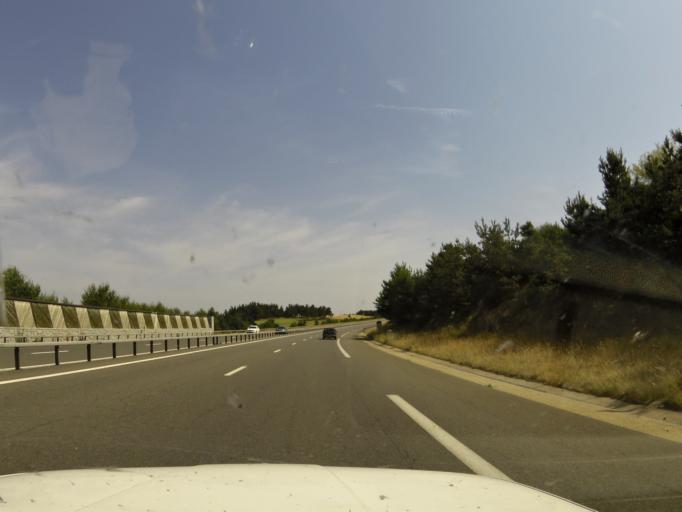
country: FR
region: Languedoc-Roussillon
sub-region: Departement de la Lozere
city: Le Malzieu-Ville
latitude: 44.8095
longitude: 3.2929
